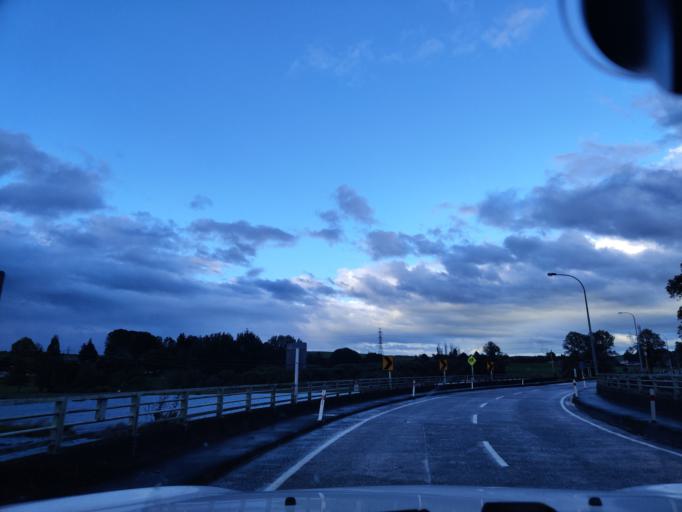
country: NZ
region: Waikato
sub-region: South Waikato District
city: Tokoroa
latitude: -38.4204
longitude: 175.8072
